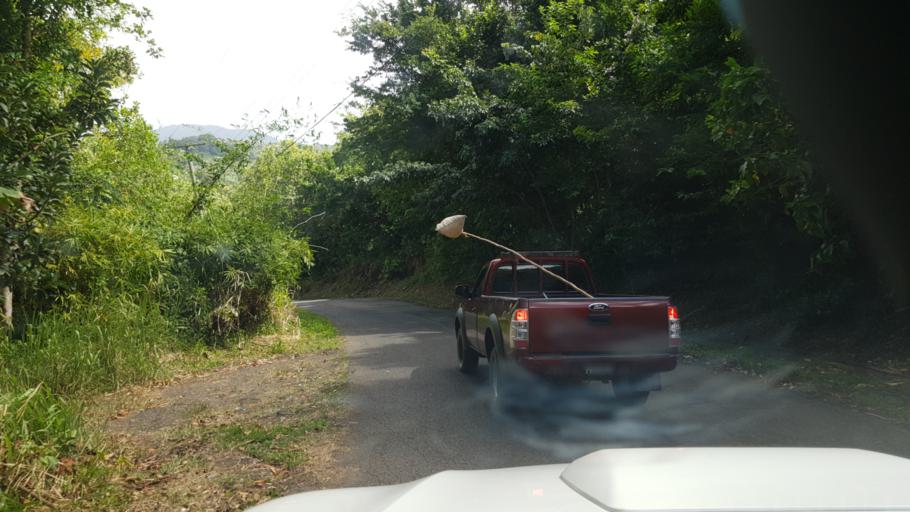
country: LC
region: Castries Quarter
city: Bisee
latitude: 14.0149
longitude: -60.9632
